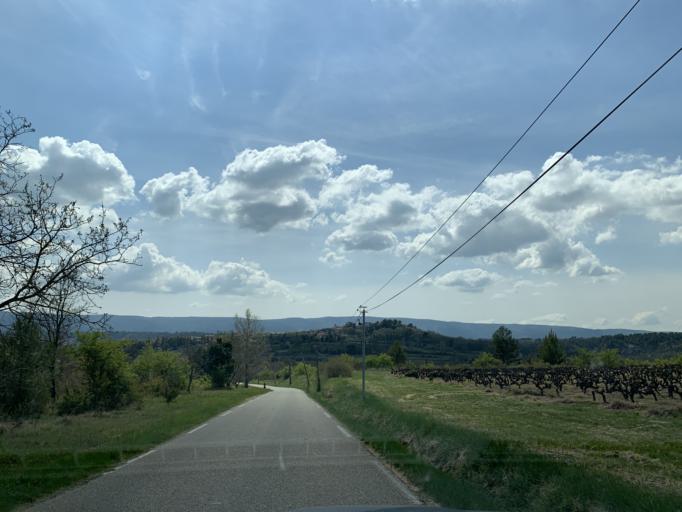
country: FR
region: Provence-Alpes-Cote d'Azur
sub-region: Departement du Vaucluse
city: Goult
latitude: 43.8731
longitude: 5.2501
